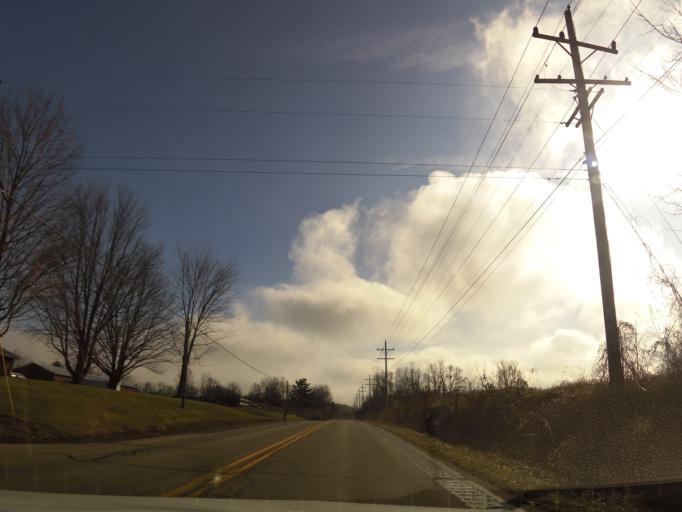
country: US
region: Indiana
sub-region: Jefferson County
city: North Madison
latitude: 38.8384
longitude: -85.4882
